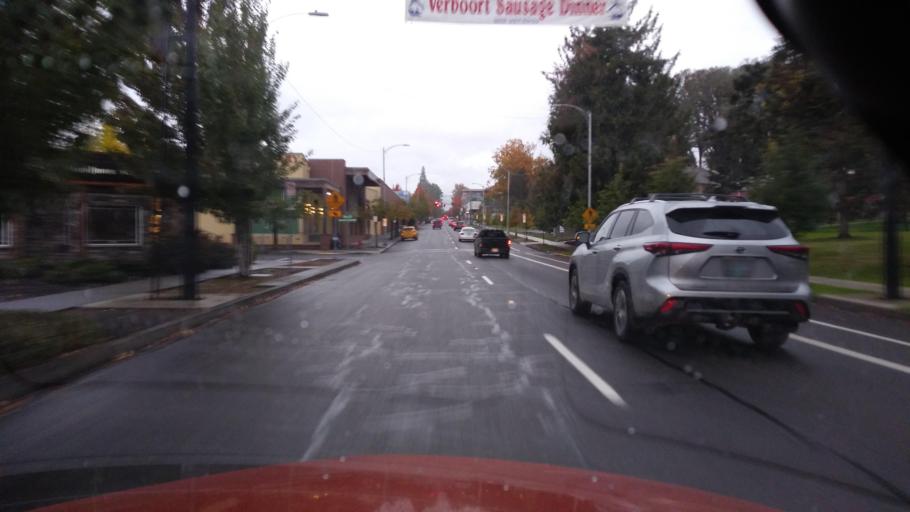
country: US
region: Oregon
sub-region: Washington County
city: Forest Grove
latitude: 45.5197
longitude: -123.1078
